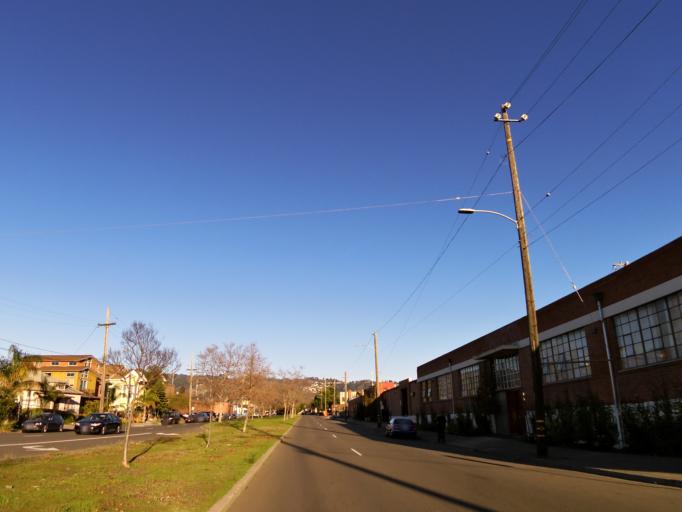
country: US
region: California
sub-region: Alameda County
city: Emeryville
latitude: 37.8426
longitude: -122.2788
